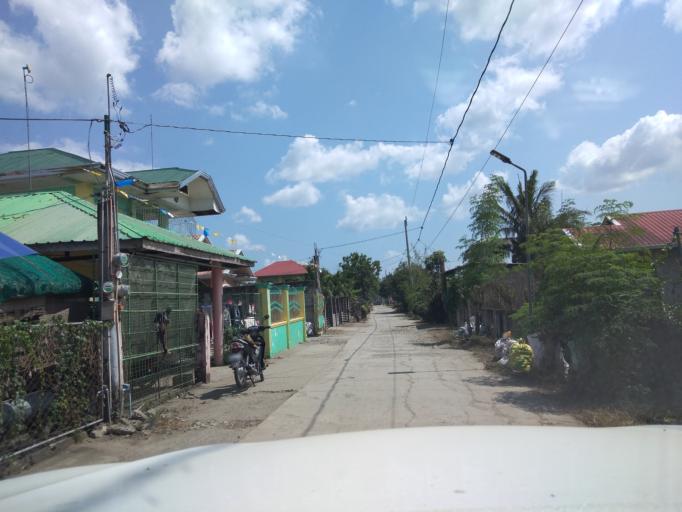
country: PH
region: Central Luzon
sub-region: Province of Pampanga
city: Bahay Pare
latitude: 15.0442
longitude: 120.8847
